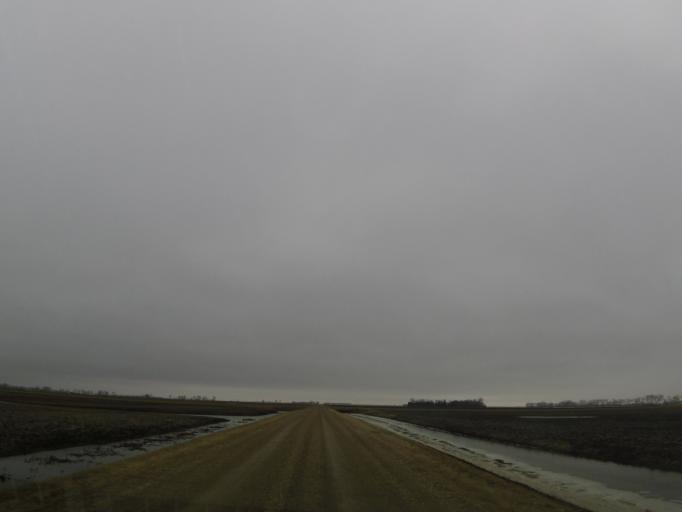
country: US
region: North Dakota
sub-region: Walsh County
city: Grafton
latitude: 48.3831
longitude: -97.2094
